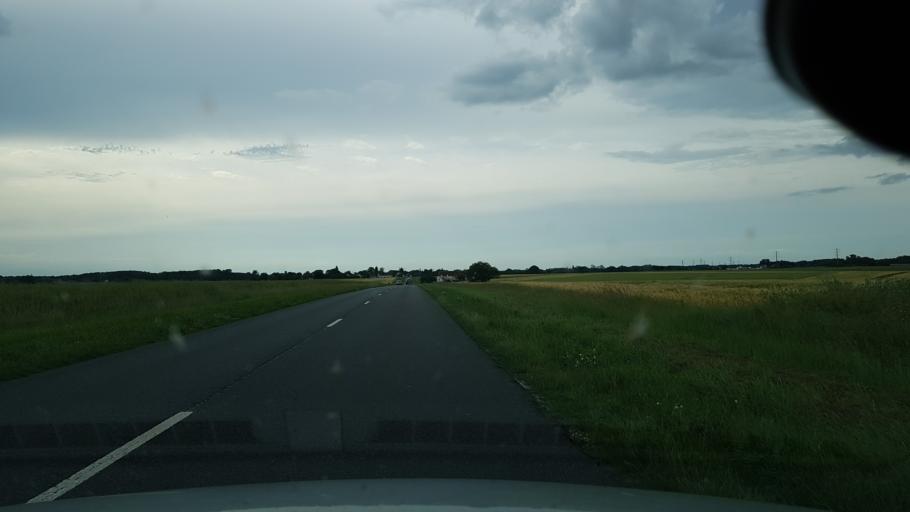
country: FR
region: Centre
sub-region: Departement du Loir-et-Cher
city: Chatillon-sur-Cher
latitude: 47.2968
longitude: 1.5192
